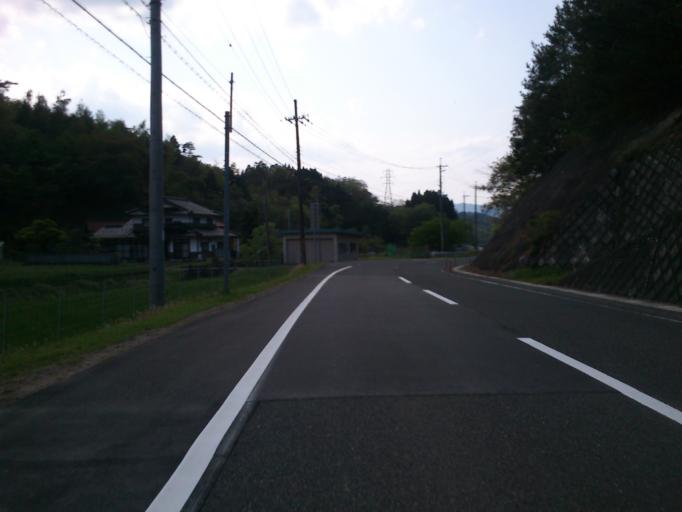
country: JP
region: Kyoto
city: Fukuchiyama
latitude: 35.3131
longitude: 134.9654
